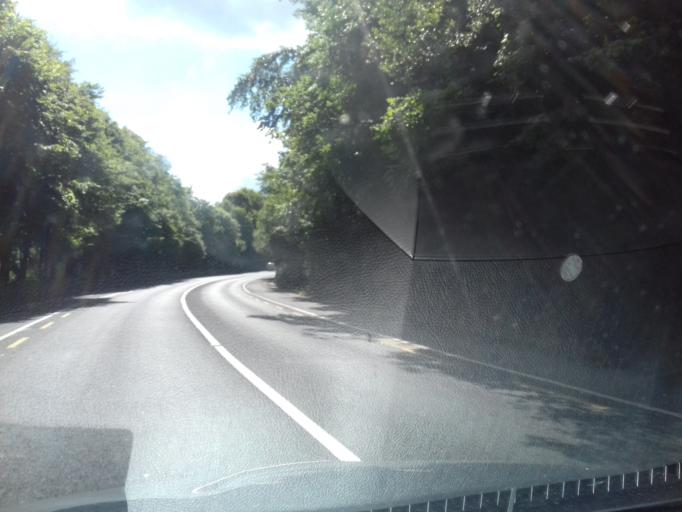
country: IE
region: Munster
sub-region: Waterford
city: Waterford
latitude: 52.2126
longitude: -7.1188
